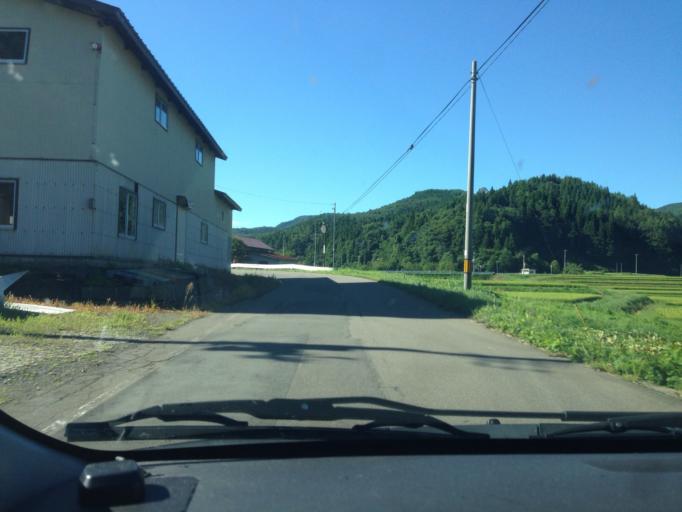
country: JP
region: Fukushima
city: Inawashiro
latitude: 37.3811
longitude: 140.0670
